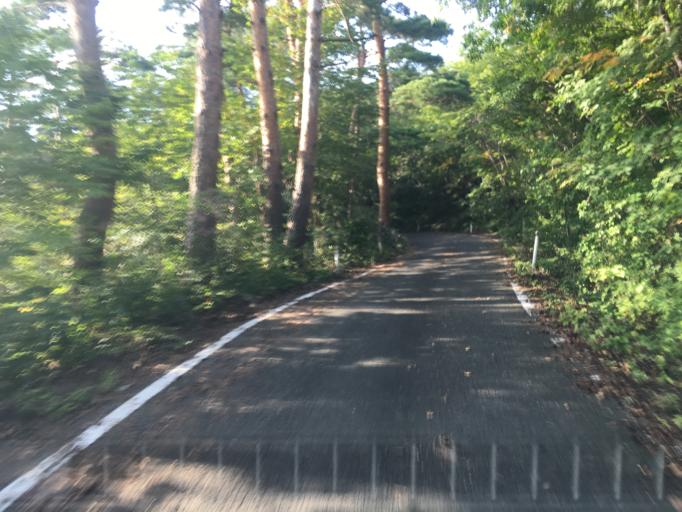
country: JP
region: Fukushima
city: Yanagawamachi-saiwaicho
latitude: 37.8978
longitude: 140.5438
